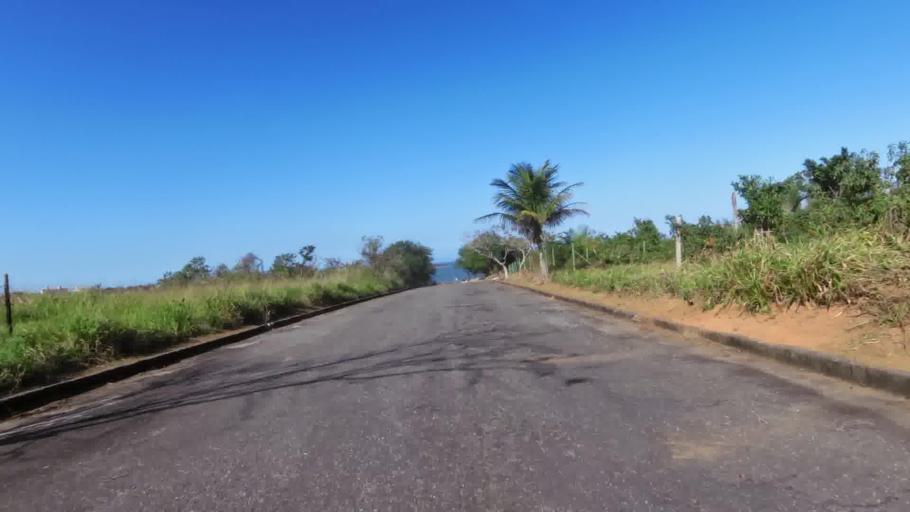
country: BR
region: Espirito Santo
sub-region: Guarapari
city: Guarapari
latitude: -20.7416
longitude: -40.5560
